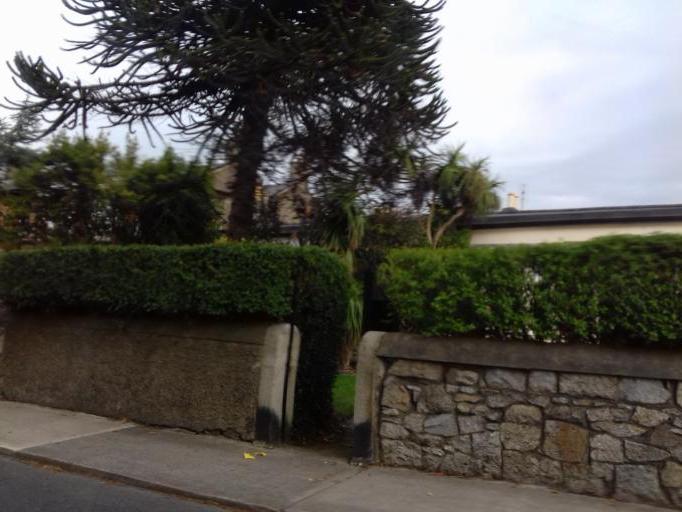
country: IE
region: Leinster
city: Dalkey
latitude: 53.2805
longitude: -6.1071
